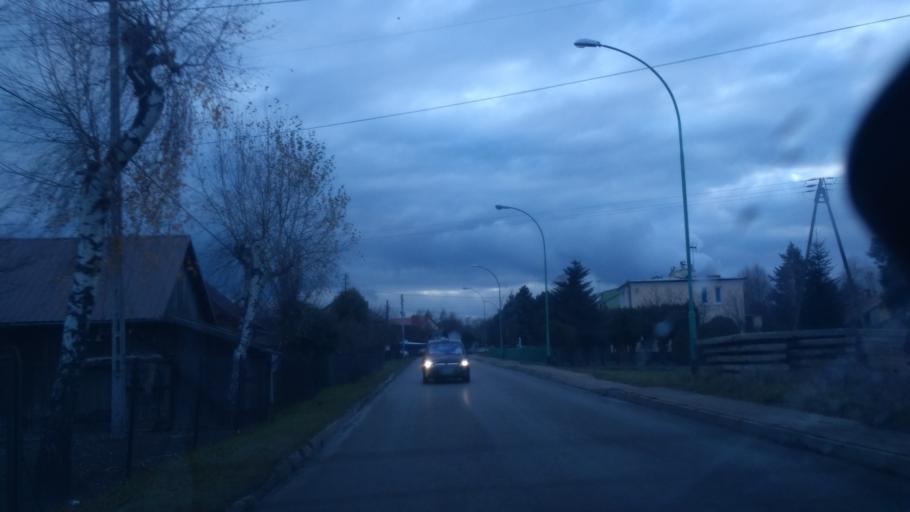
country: PL
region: Subcarpathian Voivodeship
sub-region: Powiat lancucki
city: Gluchow
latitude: 50.0928
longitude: 22.2519
